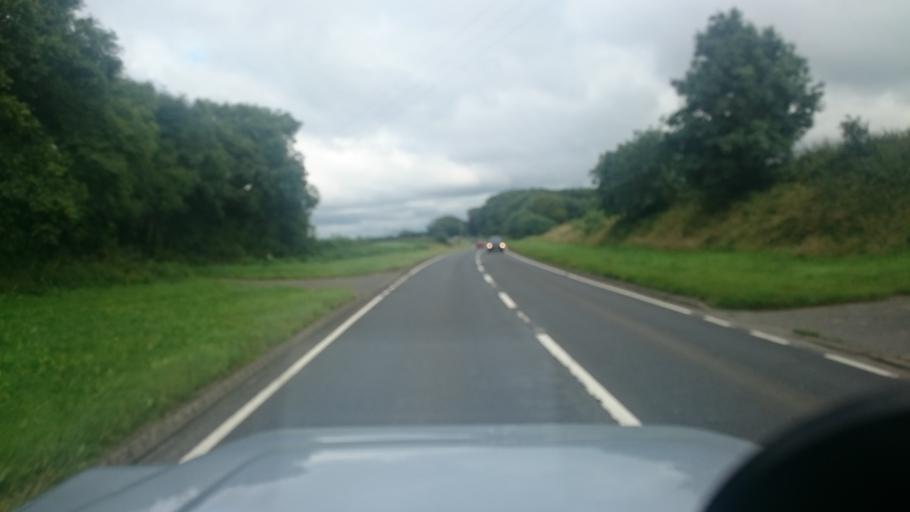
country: GB
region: Wales
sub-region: Pembrokeshire
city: Wiston
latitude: 51.8017
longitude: -4.8516
